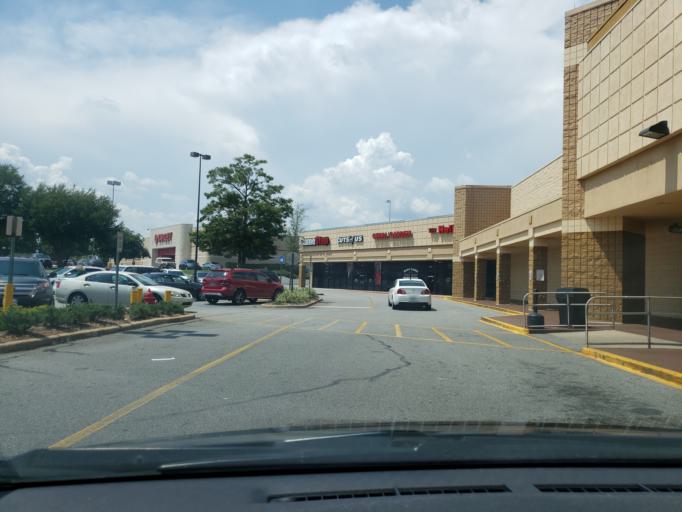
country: US
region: Georgia
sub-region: Dougherty County
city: Albany
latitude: 31.6210
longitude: -84.2235
